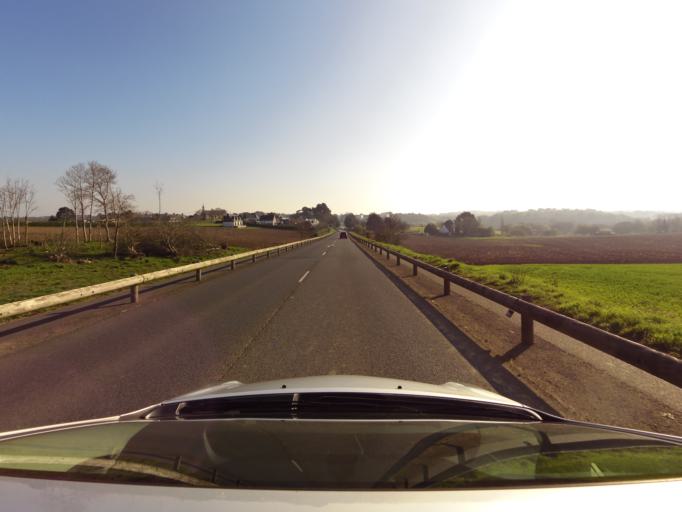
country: FR
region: Brittany
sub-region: Departement du Morbihan
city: Guidel-Plage
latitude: 47.7805
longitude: -3.5051
